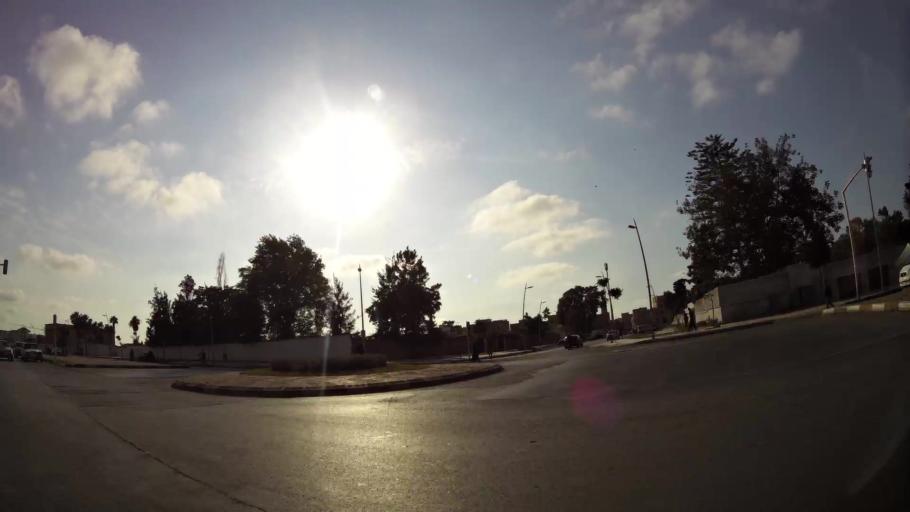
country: MA
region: Rabat-Sale-Zemmour-Zaer
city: Sale
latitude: 34.0497
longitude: -6.7849
